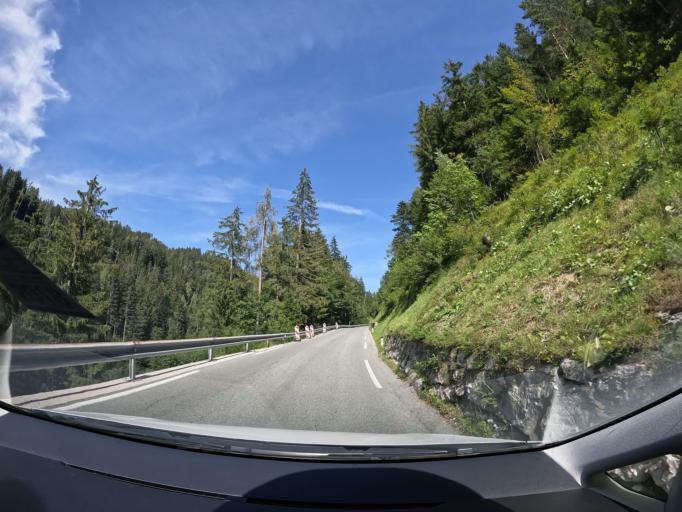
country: AT
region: Carinthia
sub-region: Politischer Bezirk Villach Land
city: Sankt Jakob
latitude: 46.5390
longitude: 14.0870
